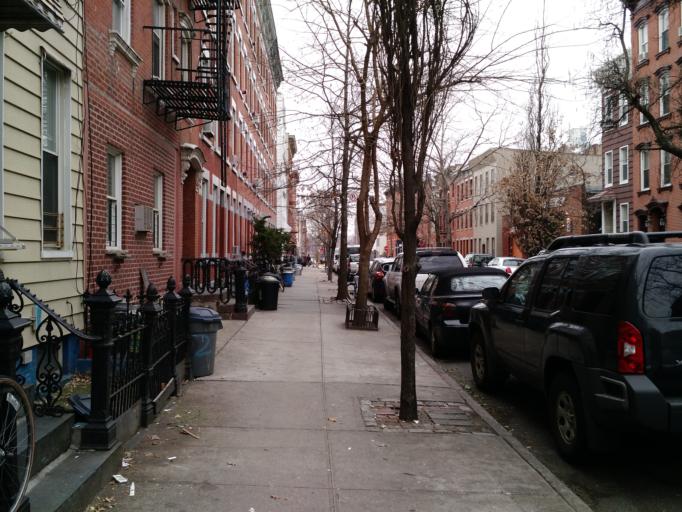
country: US
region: New York
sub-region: Queens County
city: Long Island City
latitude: 40.7195
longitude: -73.9588
